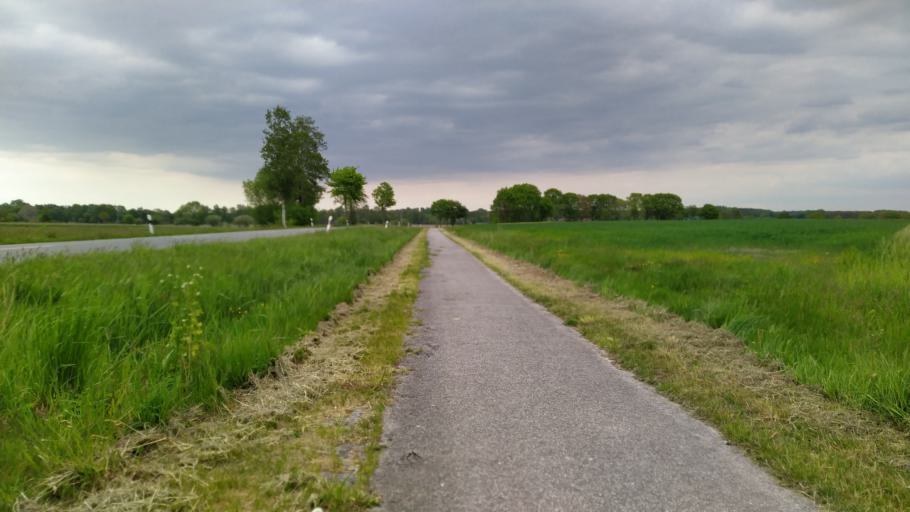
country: DE
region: Lower Saxony
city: Kirchtimke
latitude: 53.2621
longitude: 9.1872
